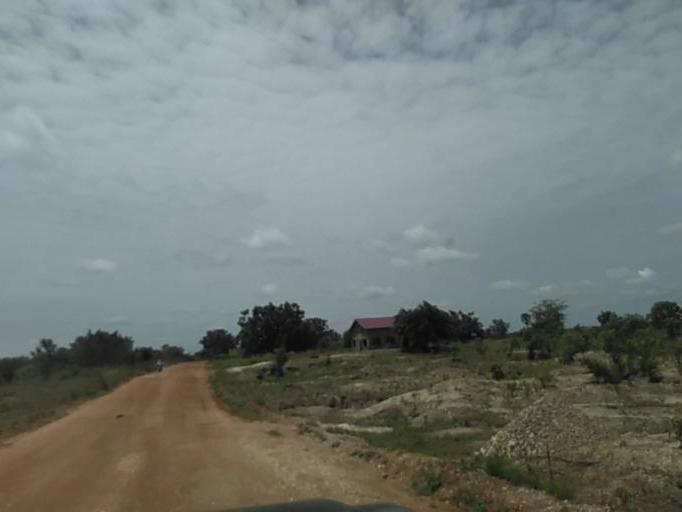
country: GH
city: Akropong
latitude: 6.0955
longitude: 0.2582
